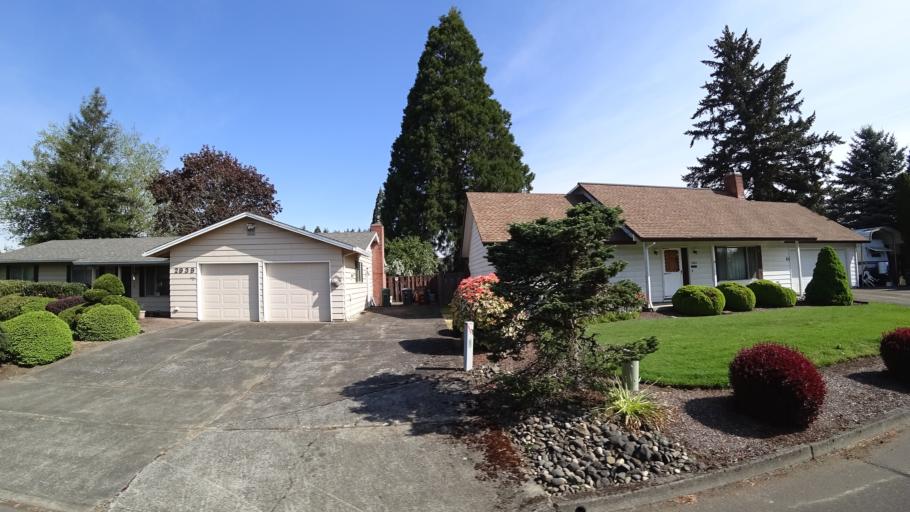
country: US
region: Oregon
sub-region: Washington County
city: Hillsboro
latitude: 45.5225
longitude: -122.9526
